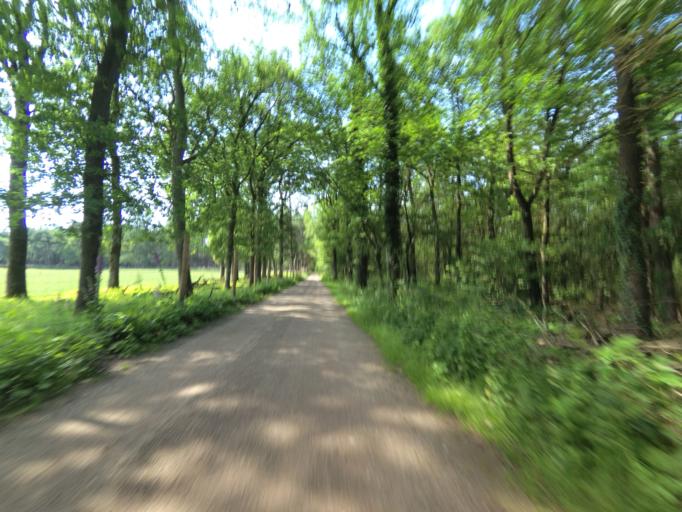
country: NL
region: Gelderland
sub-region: Gemeente Apeldoorn
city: Beekbergen
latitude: 52.1129
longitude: 5.8831
